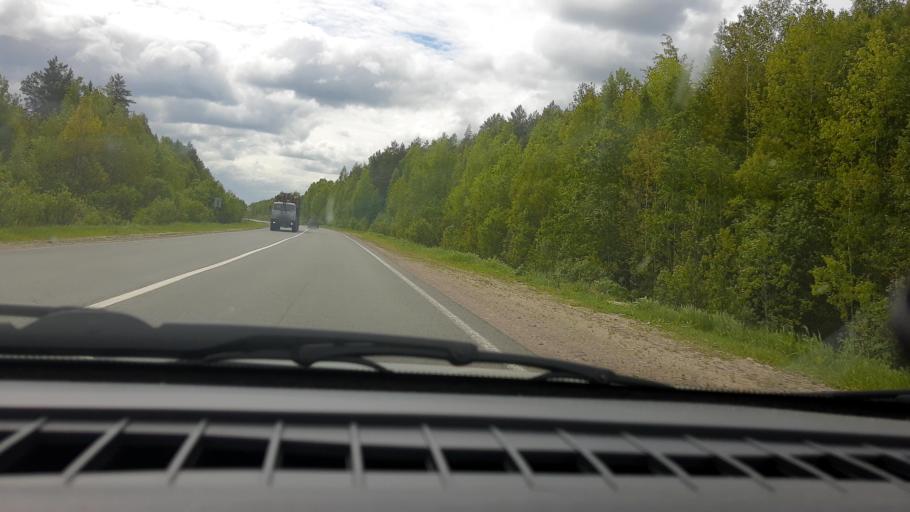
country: RU
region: Nizjnij Novgorod
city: Semenov
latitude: 56.8214
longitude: 44.4972
